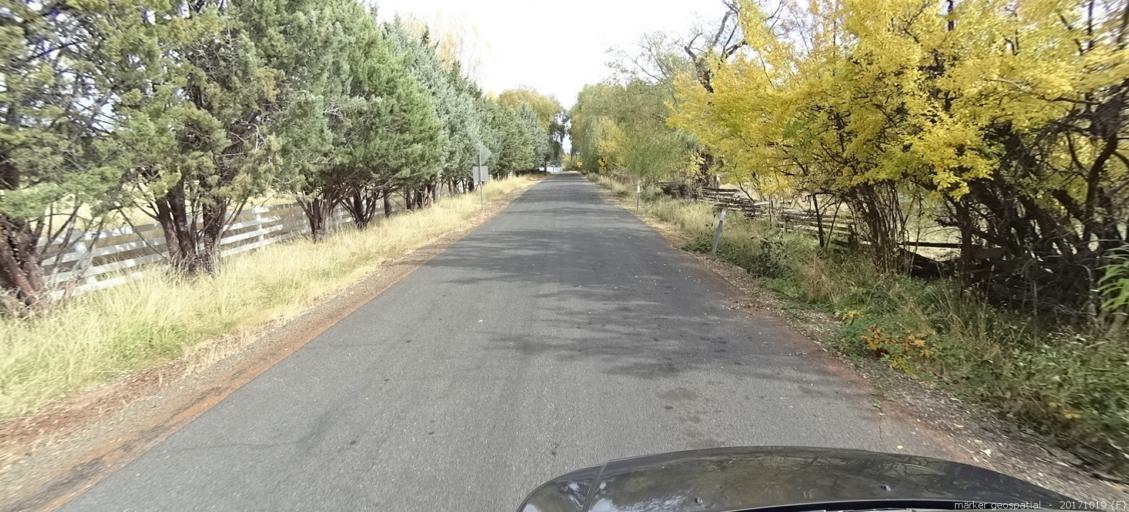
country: US
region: California
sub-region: Shasta County
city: Burney
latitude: 41.1088
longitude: -121.4941
